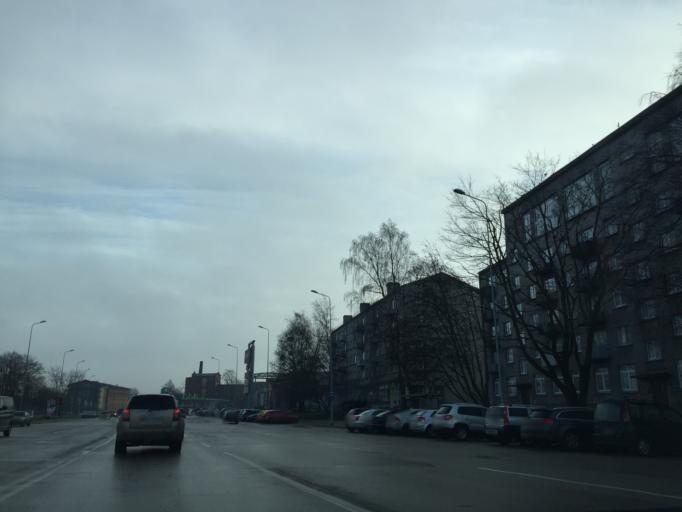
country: LV
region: Liepaja
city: Liepaja
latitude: 56.5119
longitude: 21.0149
